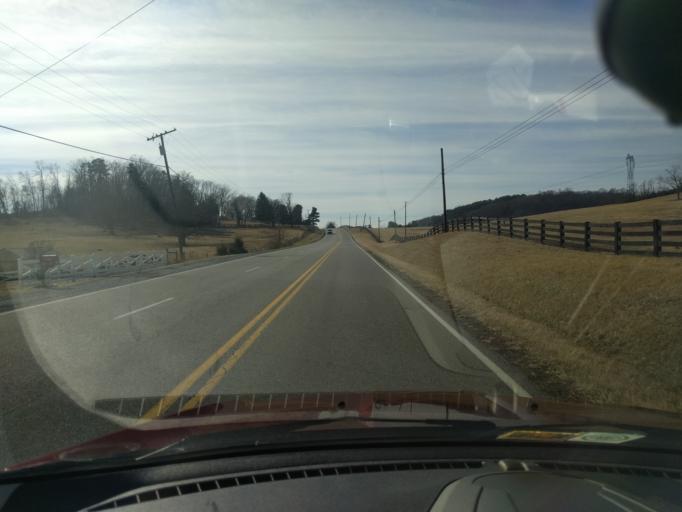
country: US
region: Virginia
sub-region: Augusta County
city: Weyers Cave
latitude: 38.2710
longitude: -78.9502
